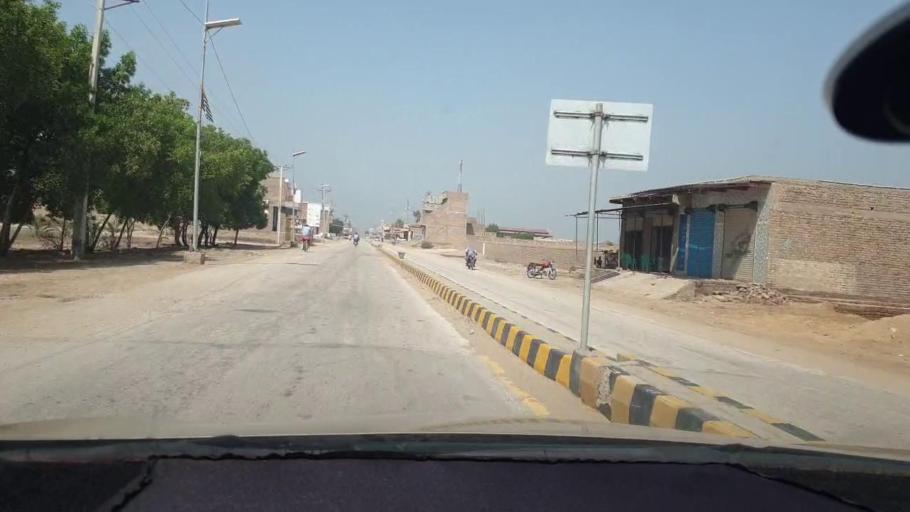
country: PK
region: Sindh
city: Kambar
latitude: 27.5889
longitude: 68.0155
